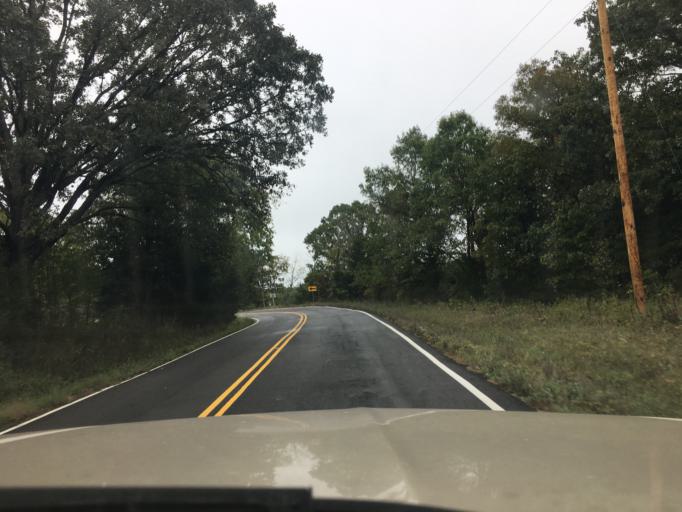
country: US
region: Missouri
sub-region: Crawford County
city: Cuba
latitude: 38.1904
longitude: -91.4810
